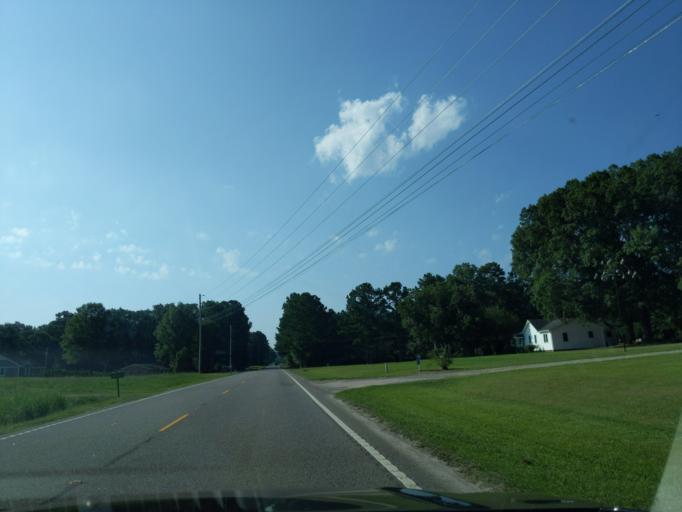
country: US
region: South Carolina
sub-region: Lexington County
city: Leesville
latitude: 34.0575
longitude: -81.5580
